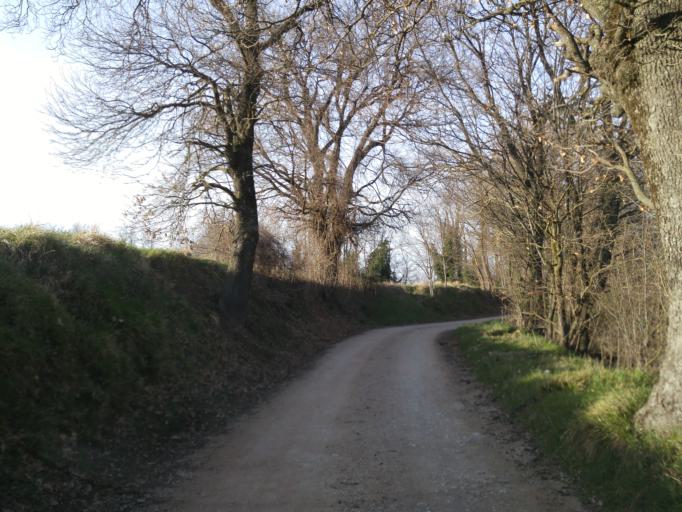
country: IT
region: The Marches
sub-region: Provincia di Pesaro e Urbino
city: Canavaccio
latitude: 43.6861
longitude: 12.6861
